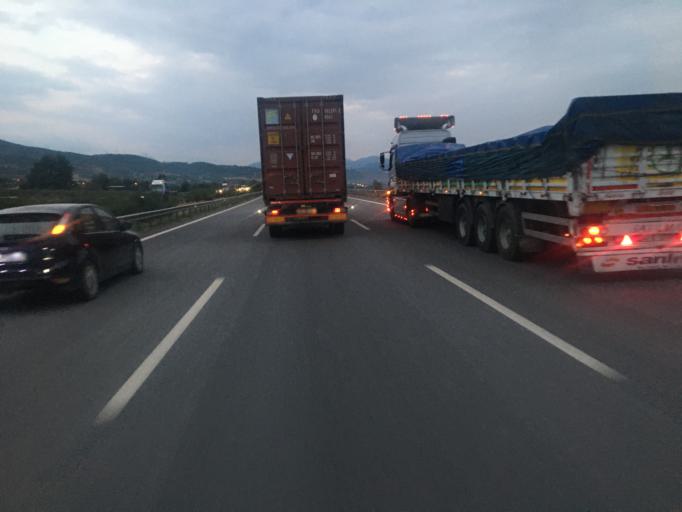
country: TR
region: Osmaniye
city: Osmaniye
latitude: 37.1339
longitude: 36.3100
